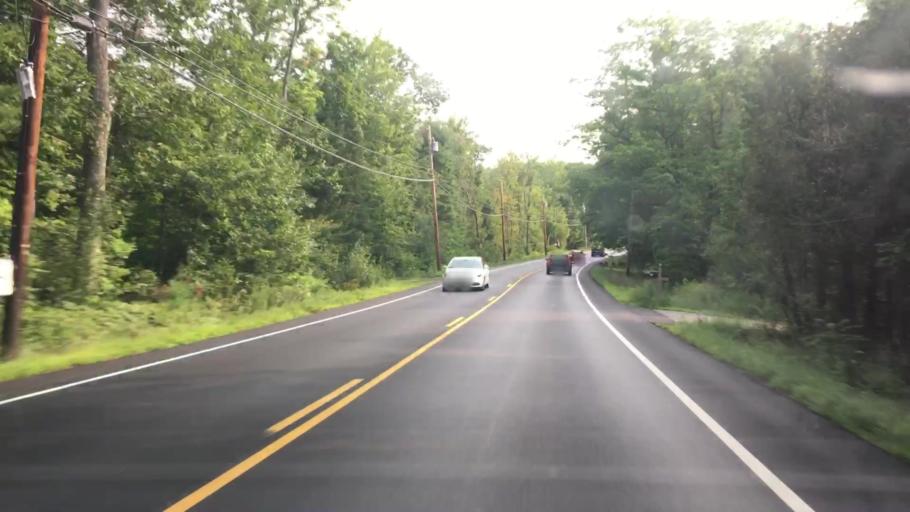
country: US
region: Maine
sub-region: Kennebec County
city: Chelsea
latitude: 44.2427
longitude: -69.7300
